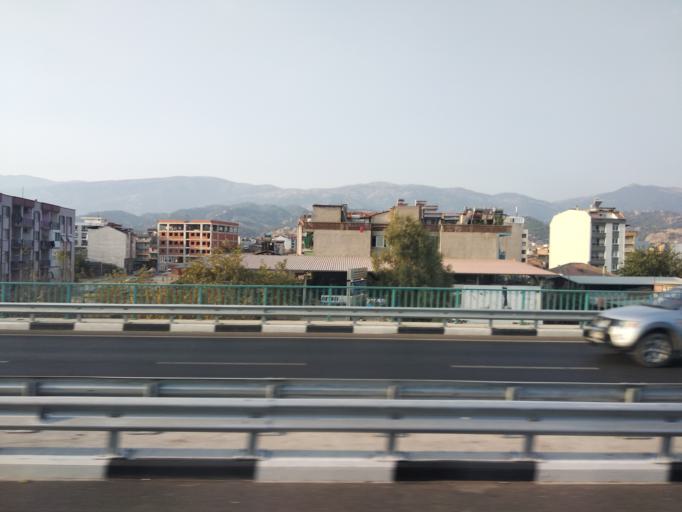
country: TR
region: Manisa
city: Salihli
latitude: 38.4903
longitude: 28.1424
